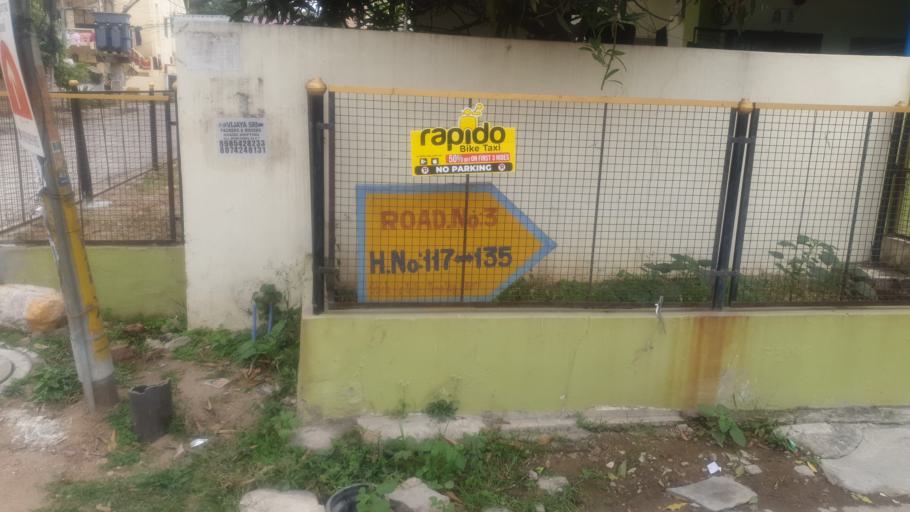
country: IN
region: Telangana
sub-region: Rangareddi
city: Kukatpalli
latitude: 17.4916
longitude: 78.3589
